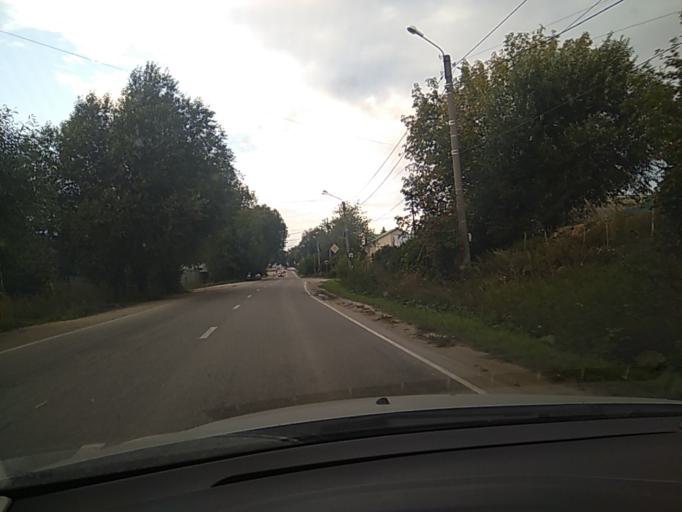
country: RU
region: Chelyabinsk
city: Kyshtym
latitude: 55.6980
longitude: 60.5524
